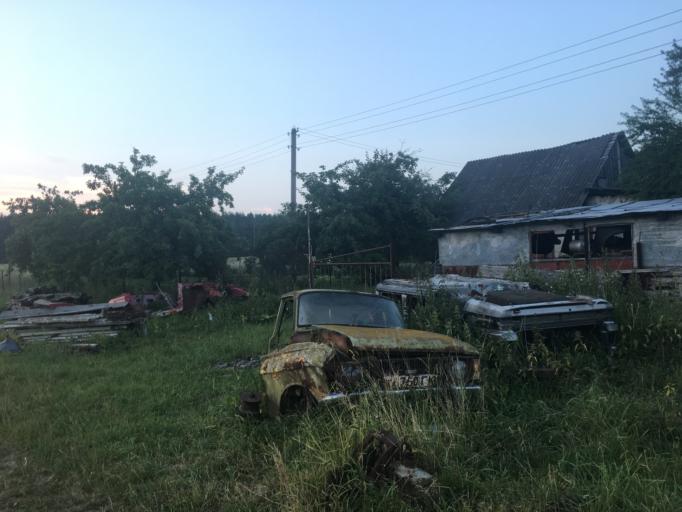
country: BY
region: Grodnenskaya
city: Hrodna
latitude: 53.7112
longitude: 23.7857
